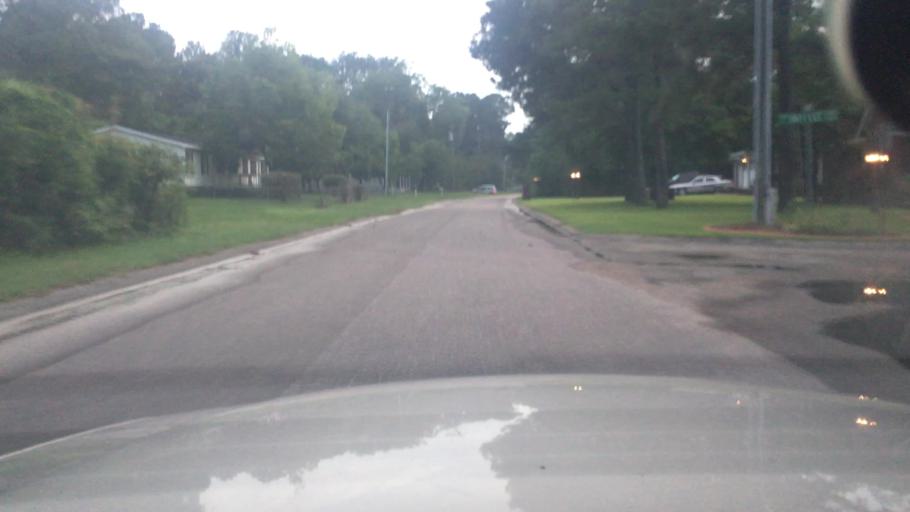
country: US
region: North Carolina
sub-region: Cumberland County
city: Hope Mills
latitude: 34.9629
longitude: -78.9334
